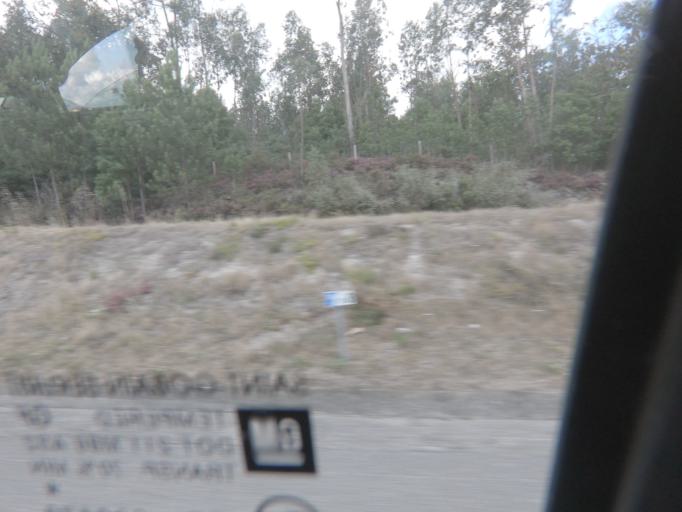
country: PT
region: Porto
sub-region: Paredes
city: Baltar
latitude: 41.1878
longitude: -8.3648
